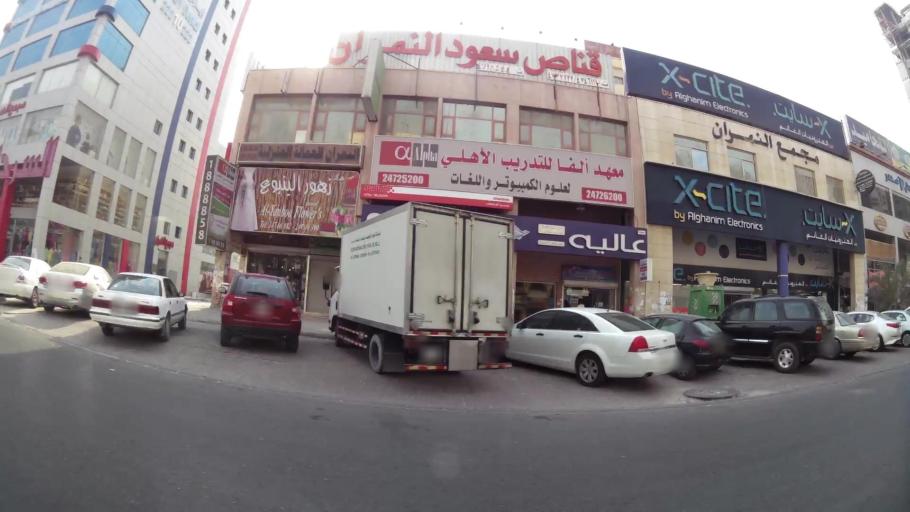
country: KW
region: Al Farwaniyah
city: Al Farwaniyah
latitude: 29.2768
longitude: 47.9627
